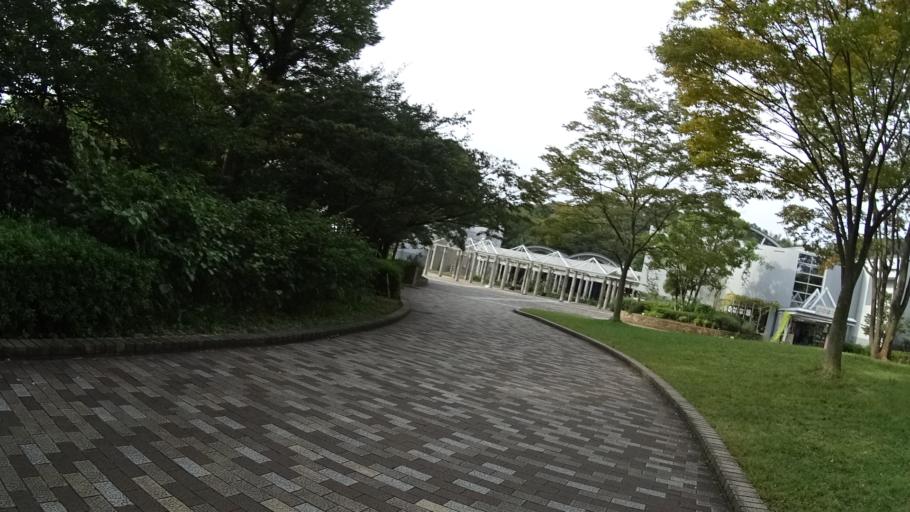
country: JP
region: Kanagawa
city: Zushi
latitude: 35.3518
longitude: 139.6008
